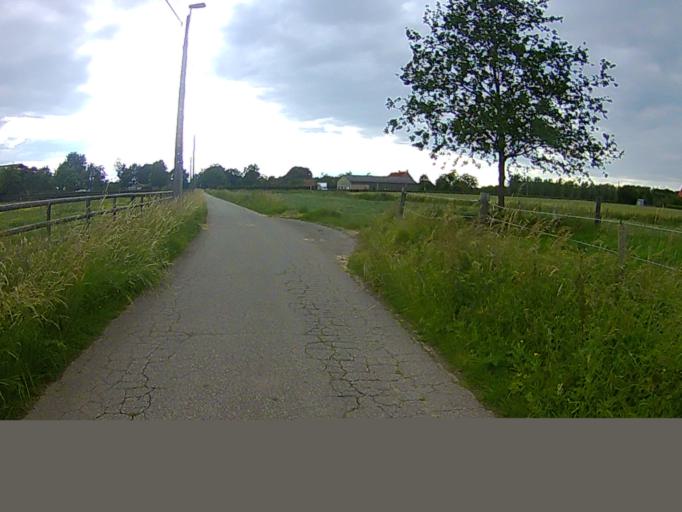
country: BE
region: Flanders
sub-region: Provincie Antwerpen
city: Ranst
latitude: 51.1632
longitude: 4.5495
